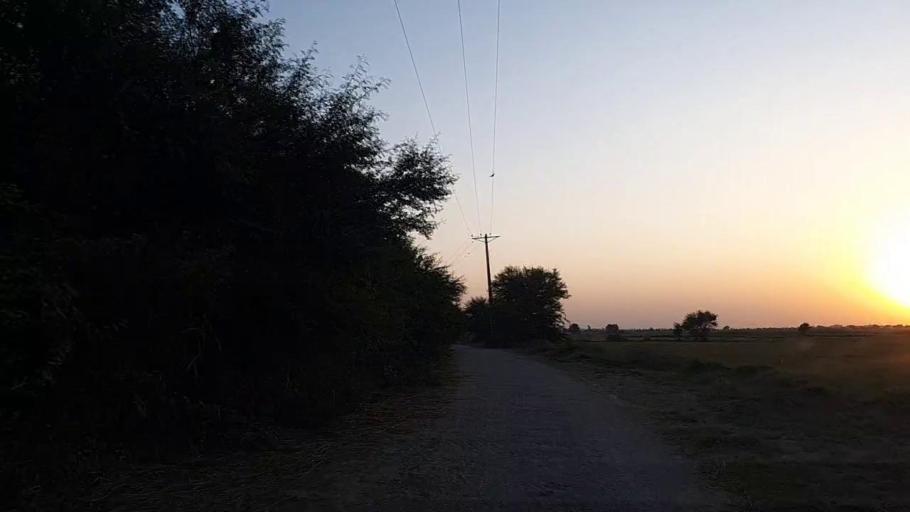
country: PK
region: Sindh
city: Mirpur Batoro
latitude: 24.6310
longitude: 68.1855
